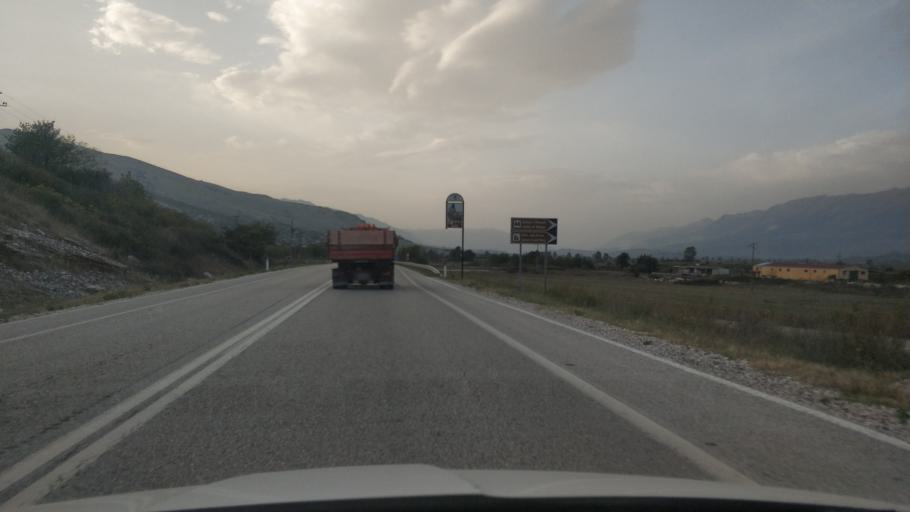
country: AL
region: Gjirokaster
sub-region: Rrethi i Gjirokastres
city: Libohove
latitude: 39.9502
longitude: 20.2565
